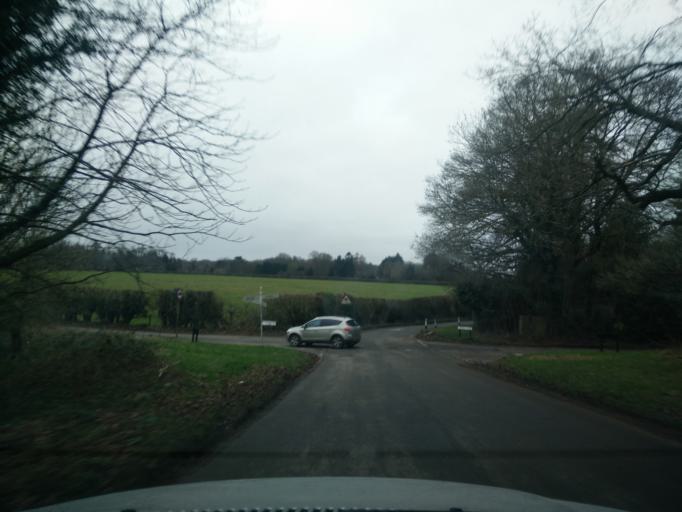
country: GB
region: England
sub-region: Buckinghamshire
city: Little Chalfont
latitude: 51.6518
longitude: -0.5475
